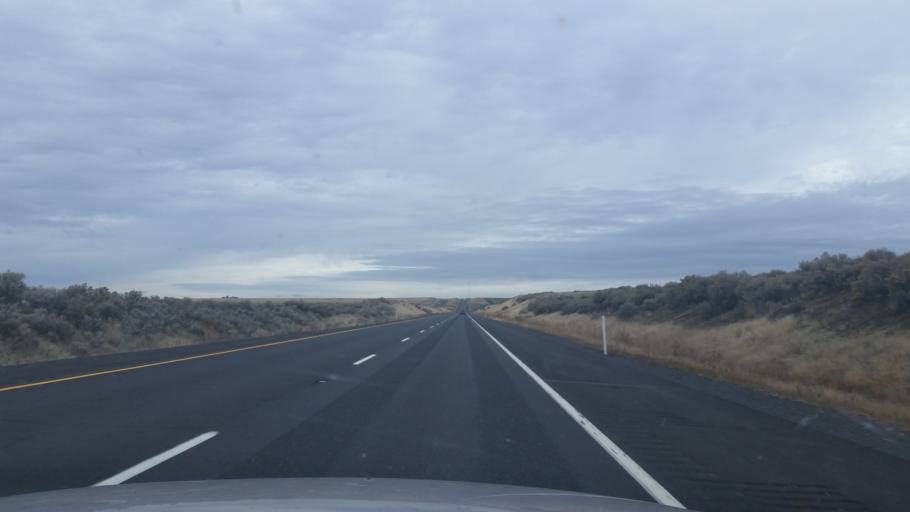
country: US
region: Washington
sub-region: Adams County
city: Ritzville
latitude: 47.0968
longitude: -118.6344
